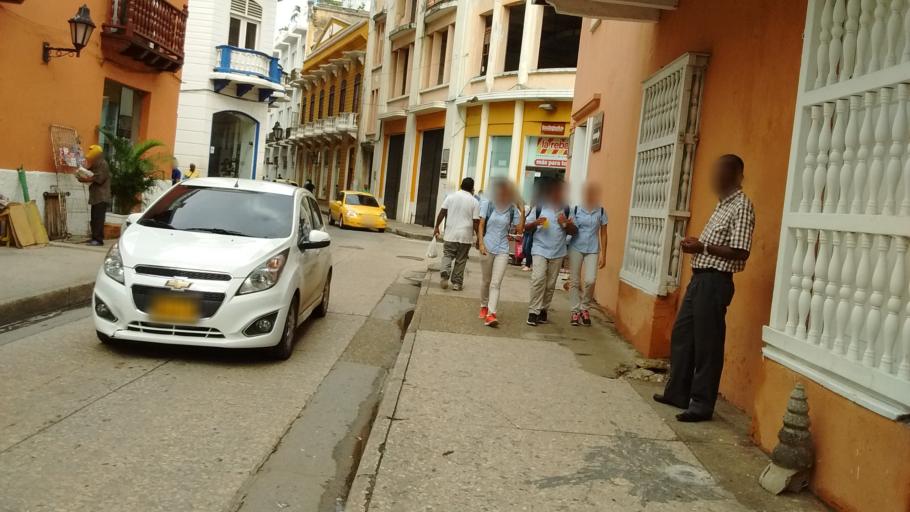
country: CO
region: Bolivar
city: Cartagena
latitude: 10.4243
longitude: -75.5488
